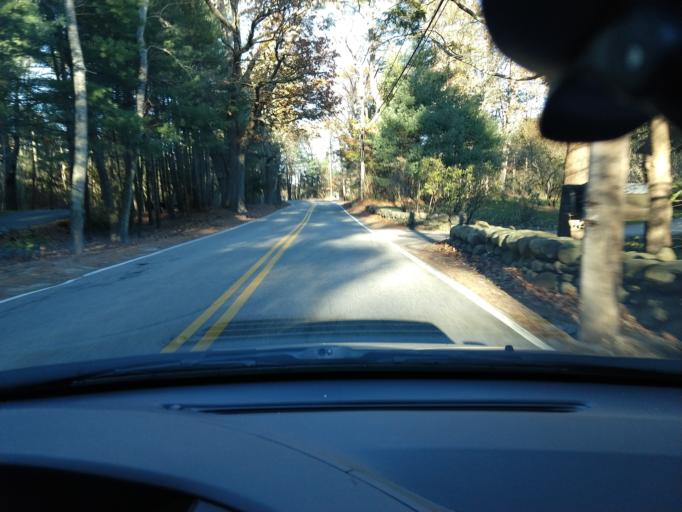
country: US
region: Massachusetts
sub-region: Middlesex County
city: Carlisle
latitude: 42.5060
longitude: -71.3262
